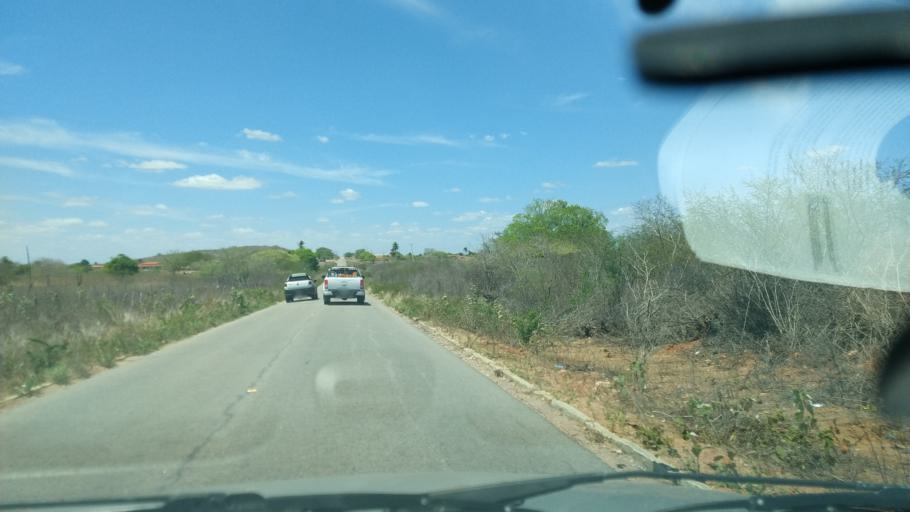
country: BR
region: Rio Grande do Norte
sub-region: Sao Paulo Do Potengi
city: Sao Paulo do Potengi
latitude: -5.9215
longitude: -35.5805
